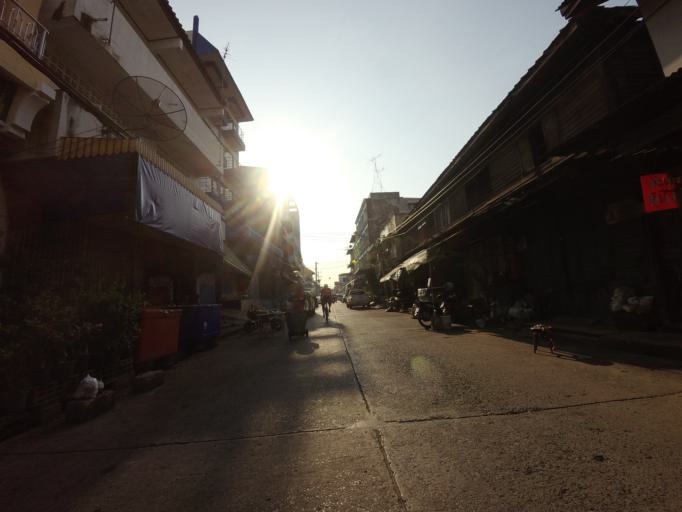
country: TH
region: Samut Sakhon
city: Samut Sakhon
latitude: 13.5463
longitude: 100.2781
